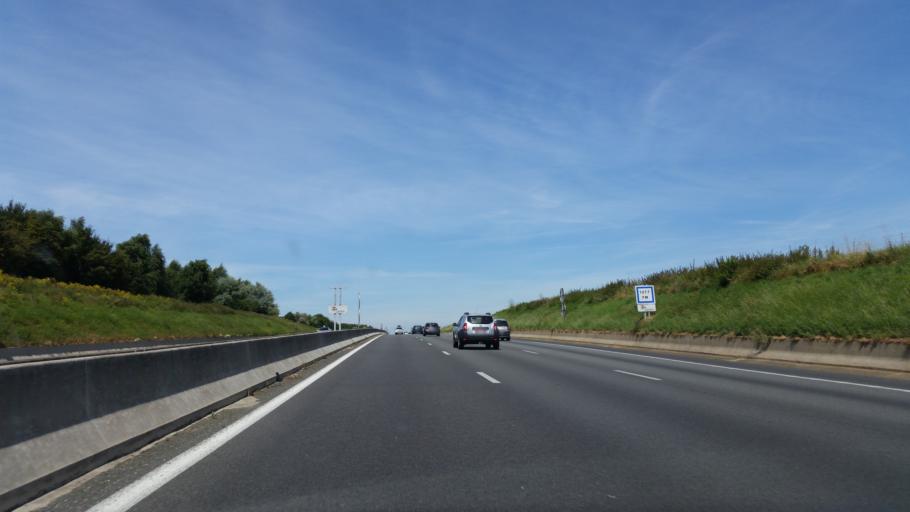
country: FR
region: Nord-Pas-de-Calais
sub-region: Departement du Pas-de-Calais
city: Croisilles
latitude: 50.1993
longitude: 2.8685
